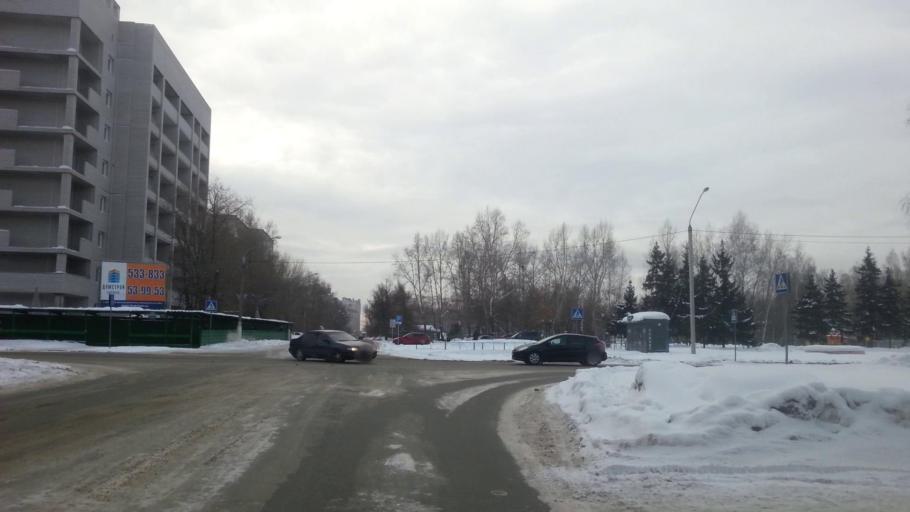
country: RU
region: Altai Krai
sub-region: Gorod Barnaulskiy
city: Barnaul
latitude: 53.3656
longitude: 83.6928
